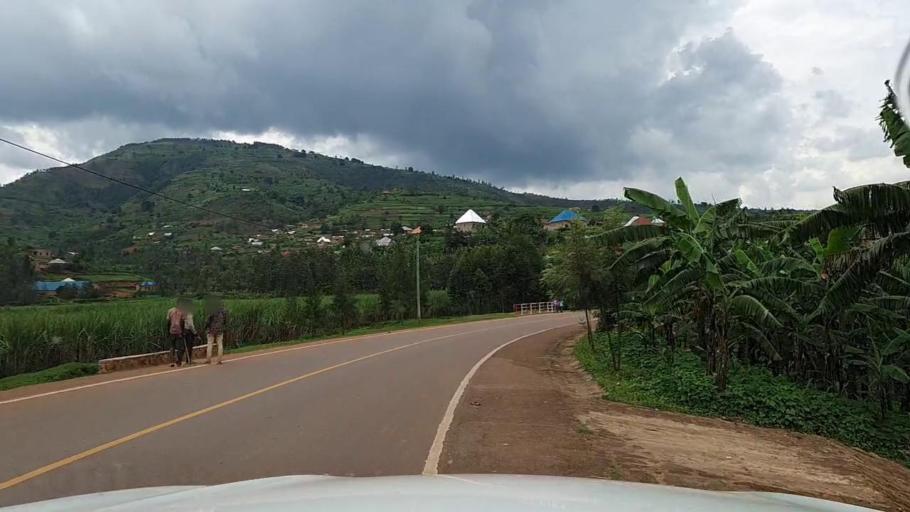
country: RW
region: Kigali
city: Kigali
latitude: -1.7717
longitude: 30.1231
